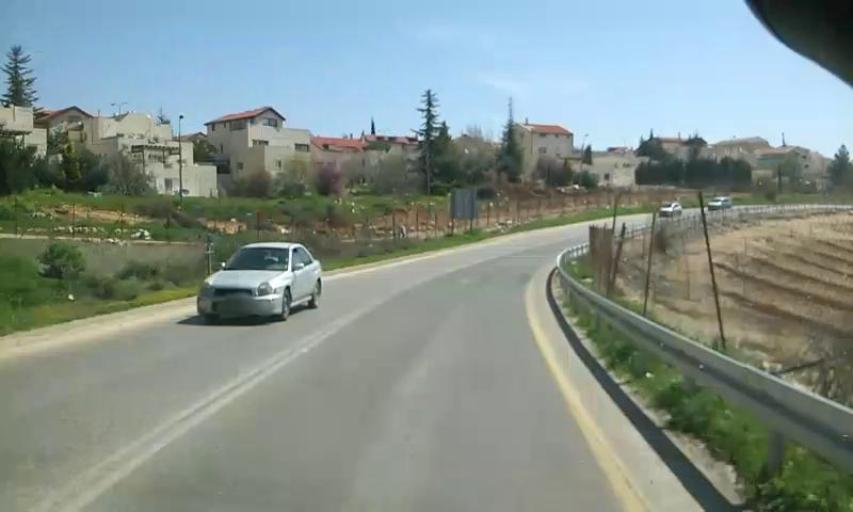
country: PS
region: West Bank
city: Nahhalin
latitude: 31.6536
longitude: 35.1247
